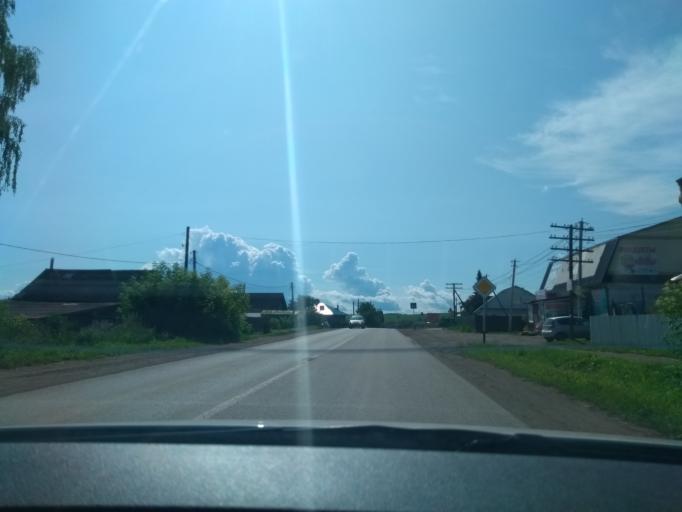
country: RU
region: Perm
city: Lobanovo
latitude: 57.8601
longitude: 56.3029
